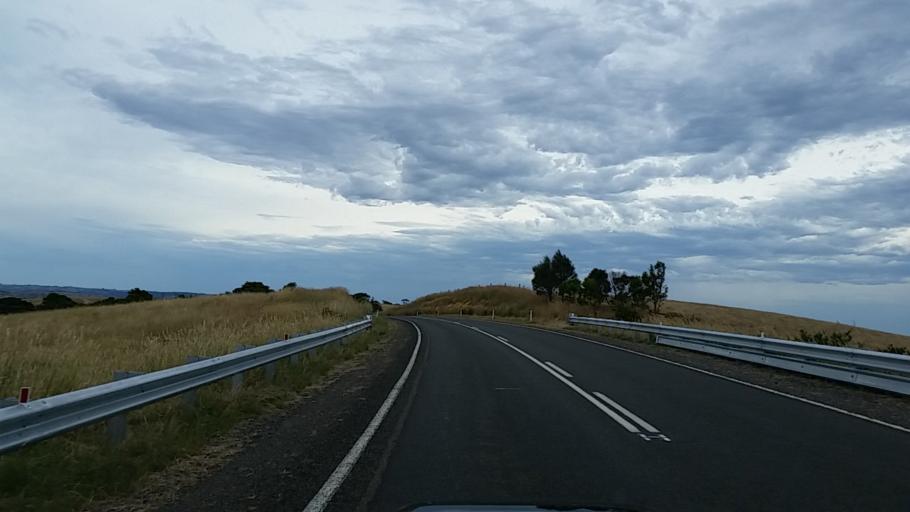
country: AU
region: South Australia
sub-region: Onkaparinga
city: Port Willunga
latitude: -35.3821
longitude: 138.4372
